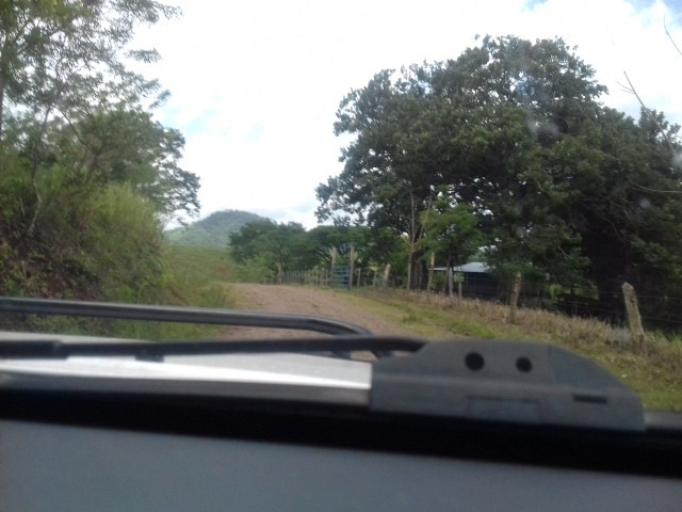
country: NI
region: Matagalpa
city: Matiguas
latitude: 13.0228
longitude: -85.4085
